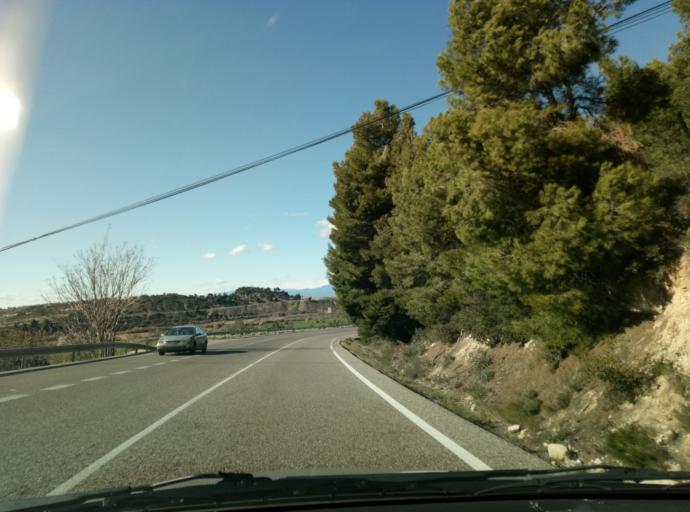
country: ES
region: Catalonia
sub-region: Provincia de Lleida
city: Ciutadilla
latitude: 41.5617
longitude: 1.1293
